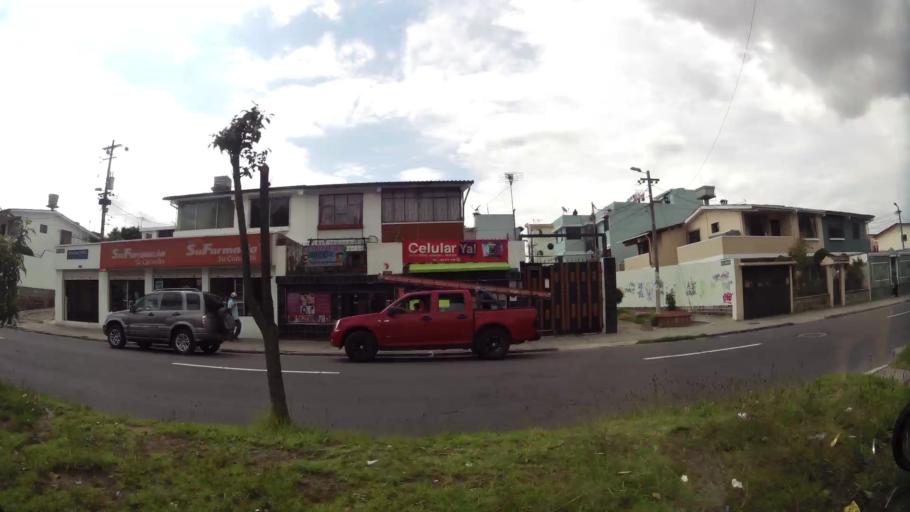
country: EC
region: Pichincha
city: Quito
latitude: -0.0914
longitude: -78.4708
